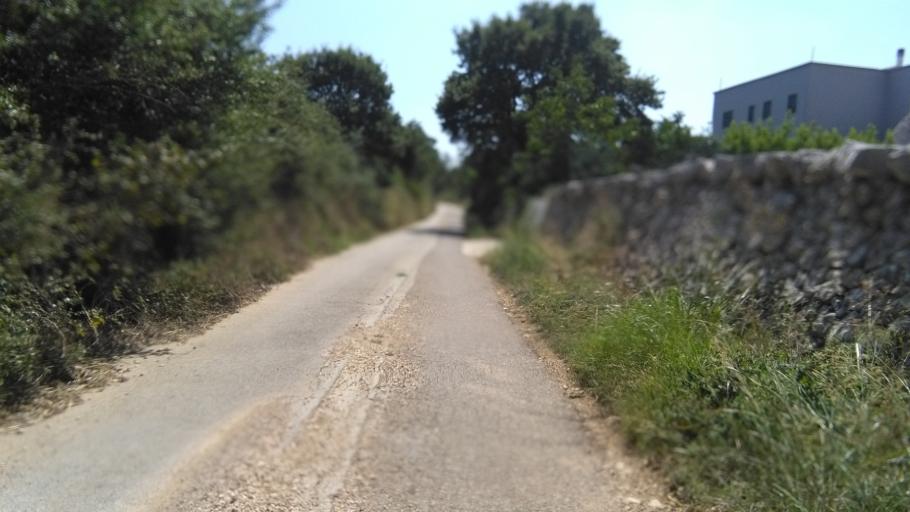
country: IT
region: Apulia
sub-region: Provincia di Bari
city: Noci
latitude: 40.8142
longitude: 17.1793
